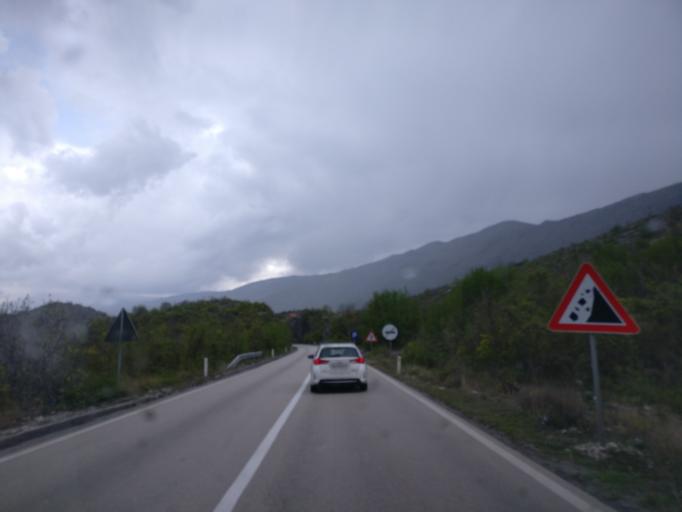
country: ME
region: Opstina Niksic
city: Niksic
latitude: 42.6937
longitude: 18.9613
